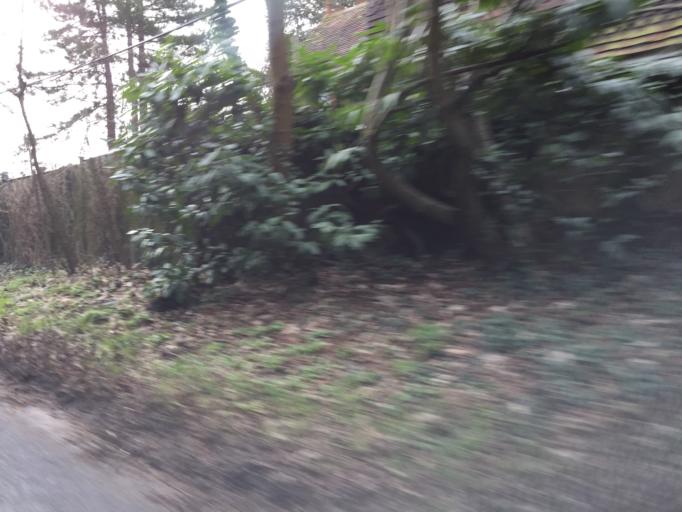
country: GB
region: England
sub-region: West Berkshire
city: Pangbourne
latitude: 51.4646
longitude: -1.0888
